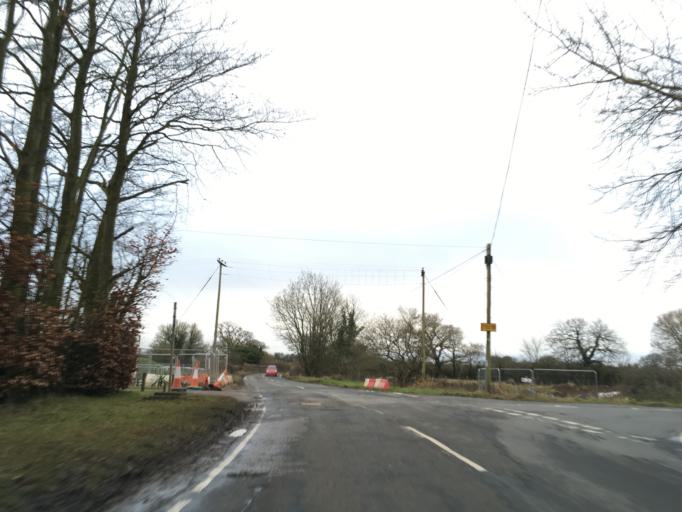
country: GB
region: England
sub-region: South Gloucestershire
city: Winterbourne
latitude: 51.5354
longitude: -2.5241
